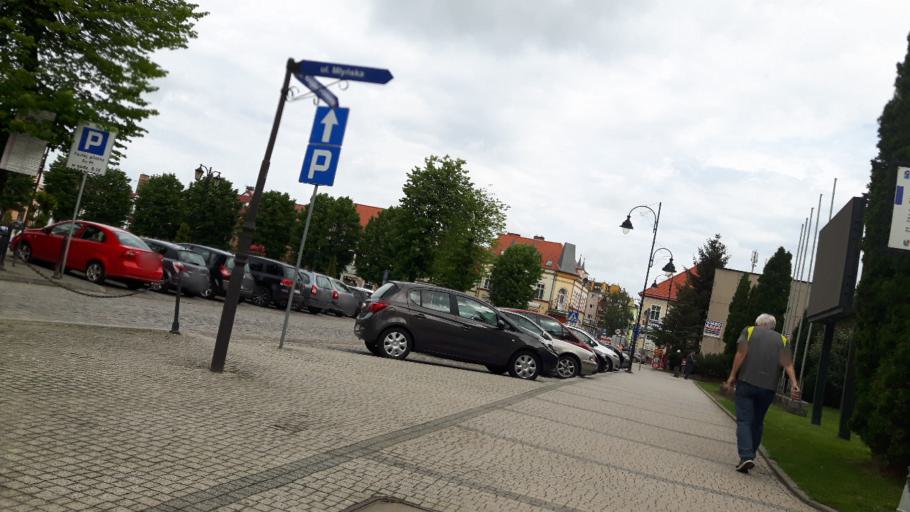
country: PL
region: West Pomeranian Voivodeship
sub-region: Powiat gryficki
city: Gryfice
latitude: 53.9141
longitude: 15.1994
